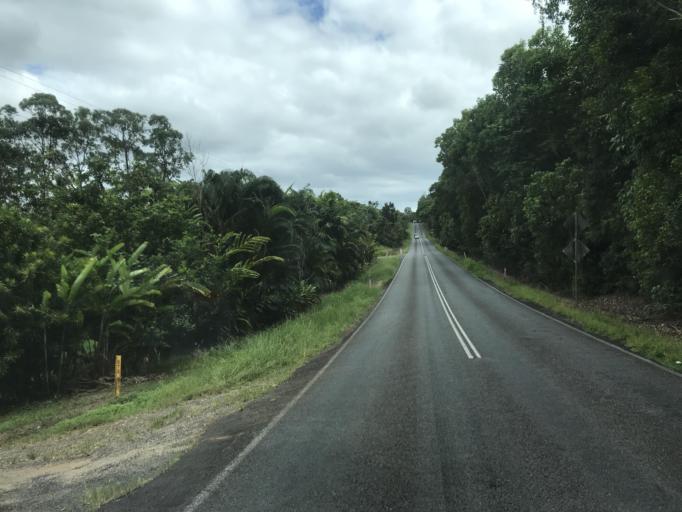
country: AU
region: Queensland
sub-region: Cassowary Coast
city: Innisfail
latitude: -17.8355
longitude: 146.0524
